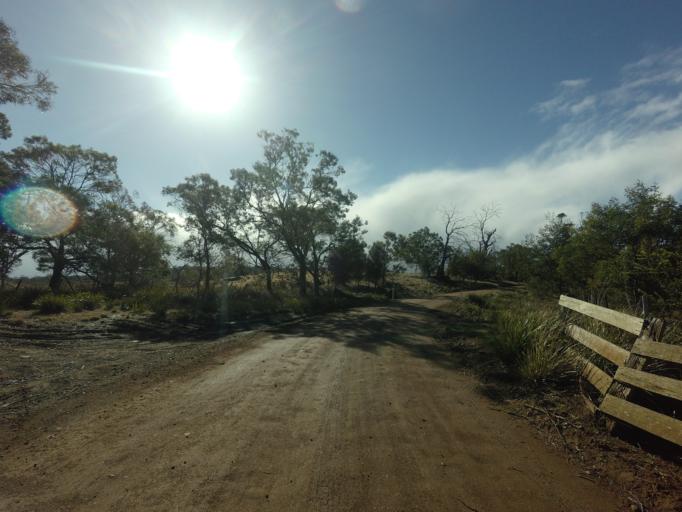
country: AU
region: Tasmania
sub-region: Sorell
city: Sorell
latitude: -42.4093
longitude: 147.9536
